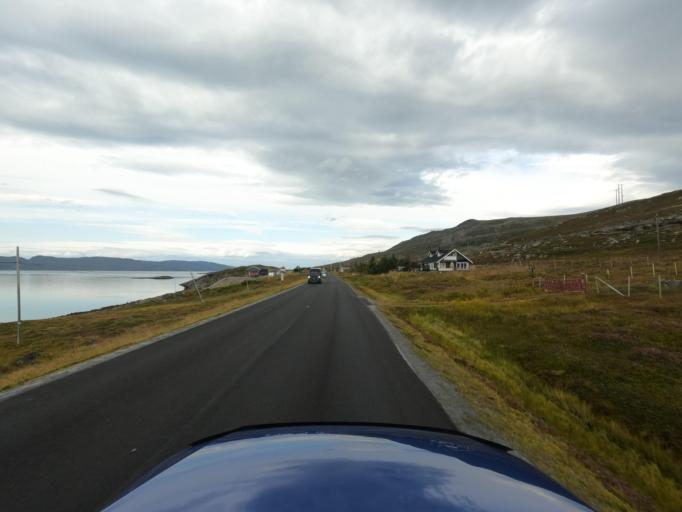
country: NO
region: Finnmark Fylke
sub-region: Hammerfest
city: Rypefjord
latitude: 70.5438
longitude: 23.7333
